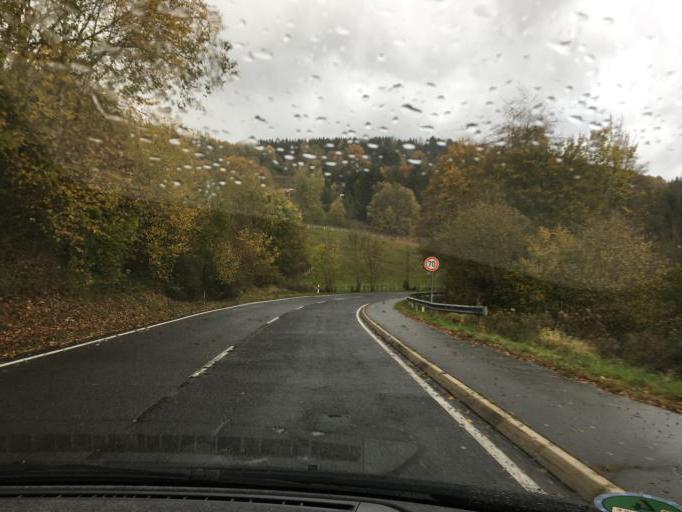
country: DE
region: North Rhine-Westphalia
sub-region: Regierungsbezirk Koln
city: Simmerath
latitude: 50.6205
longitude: 6.3747
